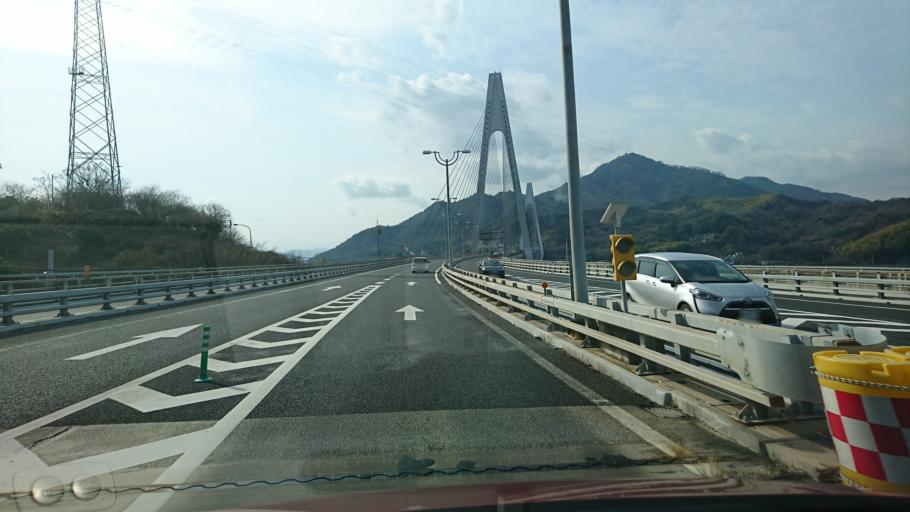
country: JP
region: Hiroshima
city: Innoshima
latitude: 34.3076
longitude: 133.1544
